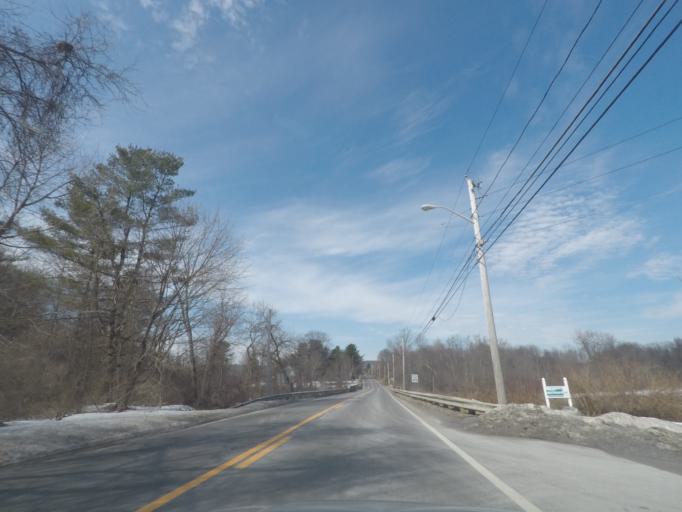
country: US
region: Massachusetts
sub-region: Berkshire County
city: West Stockbridge
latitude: 42.3413
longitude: -73.3748
